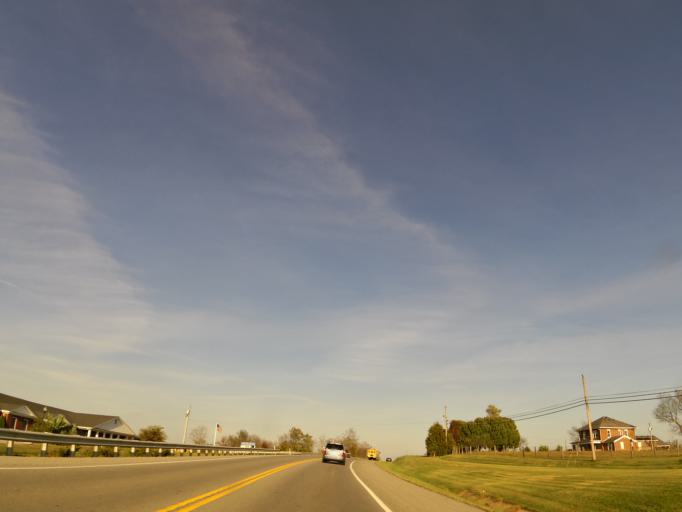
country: US
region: Kentucky
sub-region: Garrard County
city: Lancaster
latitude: 37.6032
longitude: -84.5867
